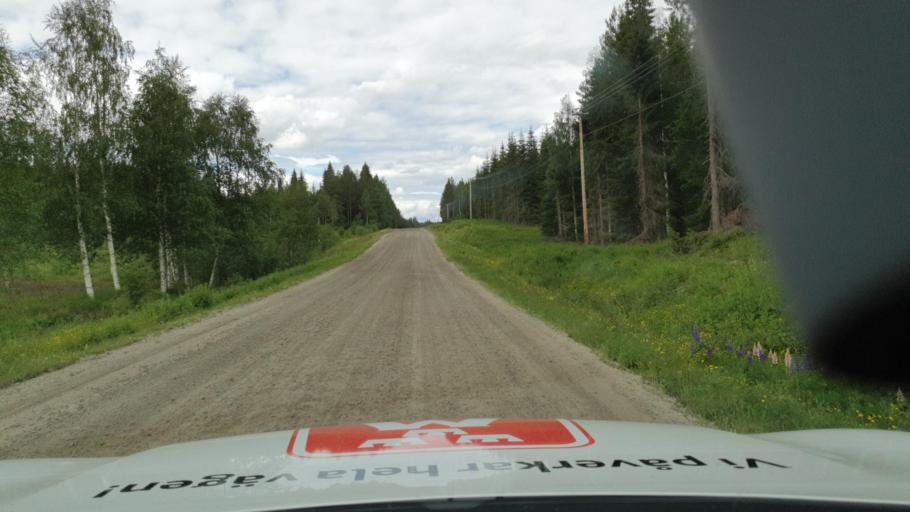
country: SE
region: Vaesterbotten
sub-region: Bjurholms Kommun
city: Bjurholm
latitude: 63.8480
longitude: 18.9862
